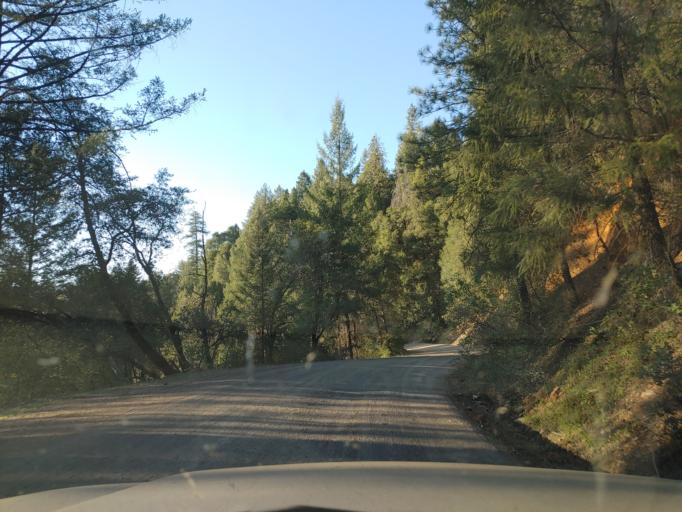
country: US
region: California
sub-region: Shasta County
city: Bella Vista
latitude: 40.8155
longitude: -122.0060
